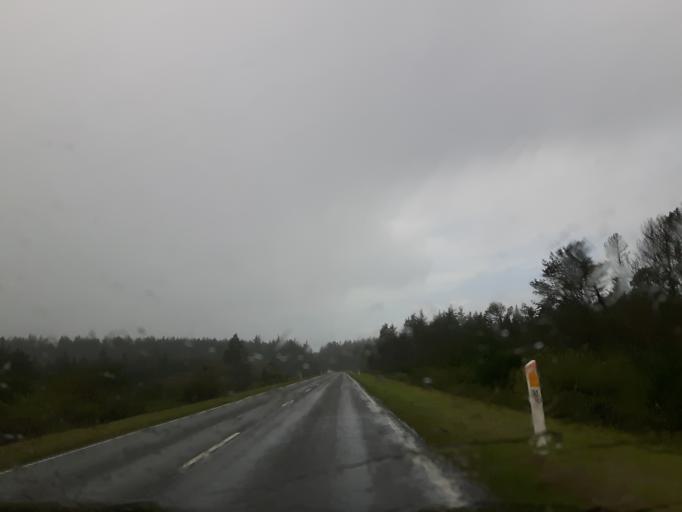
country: DK
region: North Denmark
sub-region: Thisted Kommune
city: Hanstholm
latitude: 57.0303
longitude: 8.4940
